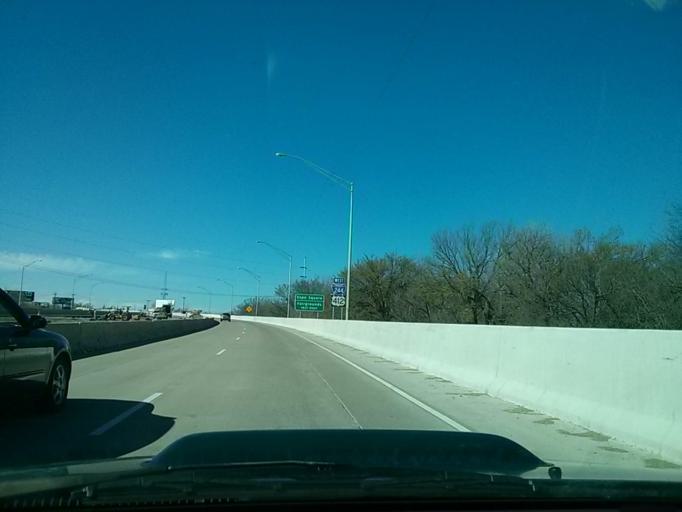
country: US
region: Oklahoma
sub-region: Tulsa County
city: Tulsa
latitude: 36.1633
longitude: -95.9104
